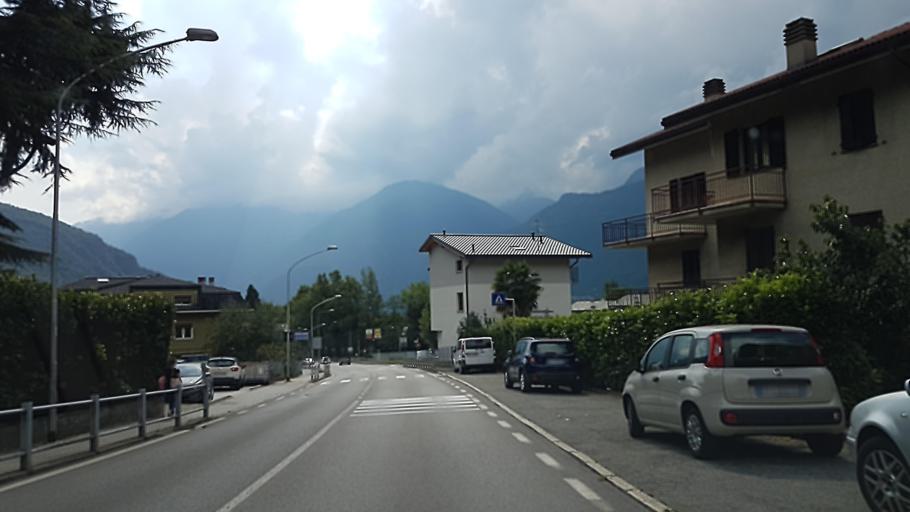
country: IT
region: Lombardy
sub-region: Provincia di Sondrio
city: Chiavenna
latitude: 46.3167
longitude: 9.3990
